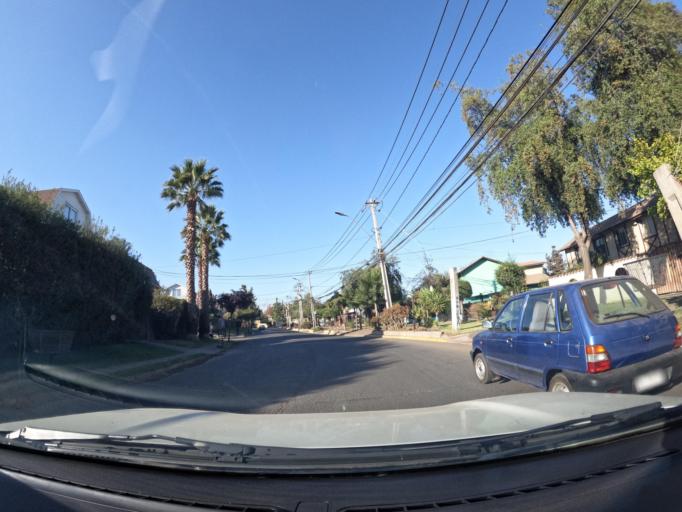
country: CL
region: Santiago Metropolitan
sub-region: Provincia de Santiago
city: Villa Presidente Frei, Nunoa, Santiago, Chile
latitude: -33.4808
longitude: -70.5392
